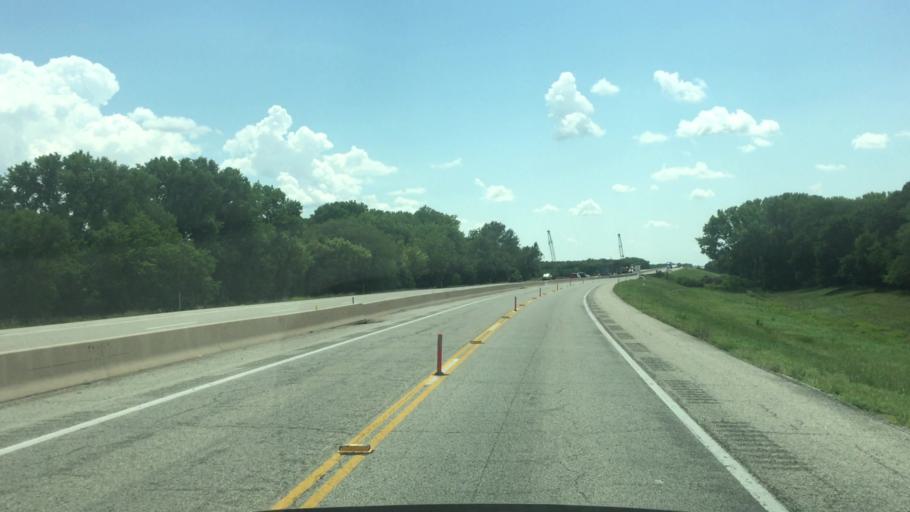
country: US
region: Kansas
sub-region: Lyon County
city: Emporia
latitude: 38.4563
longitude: -96.1966
